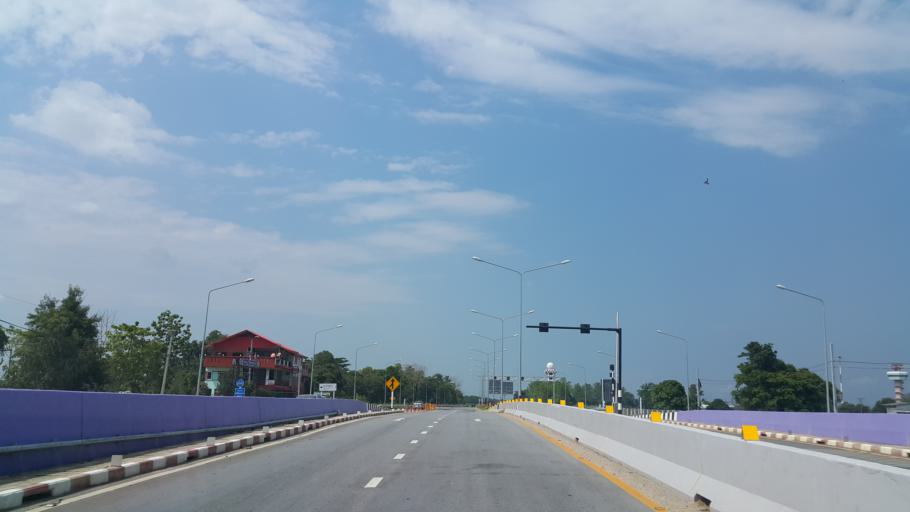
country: TH
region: Chiang Rai
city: Chiang Rai
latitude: 19.9647
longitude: 99.8828
